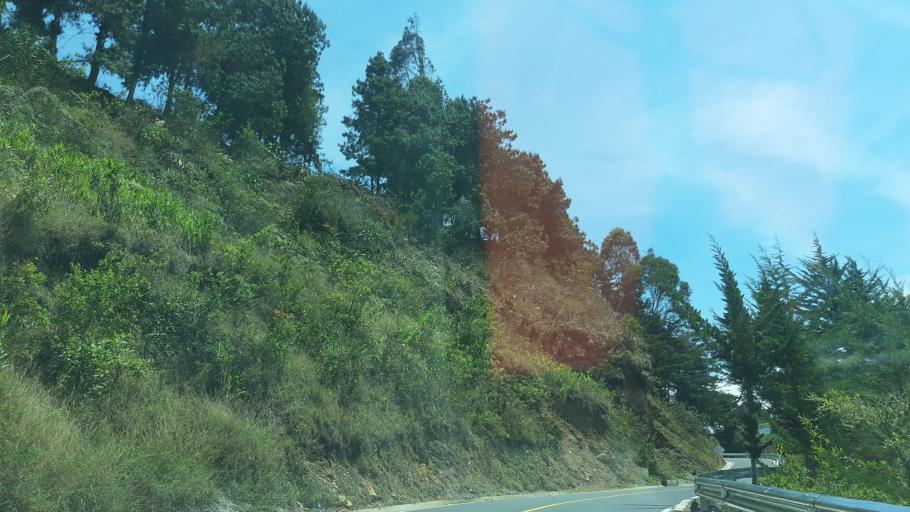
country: CO
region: Boyaca
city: Chinavita
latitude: 5.1335
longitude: -73.3885
